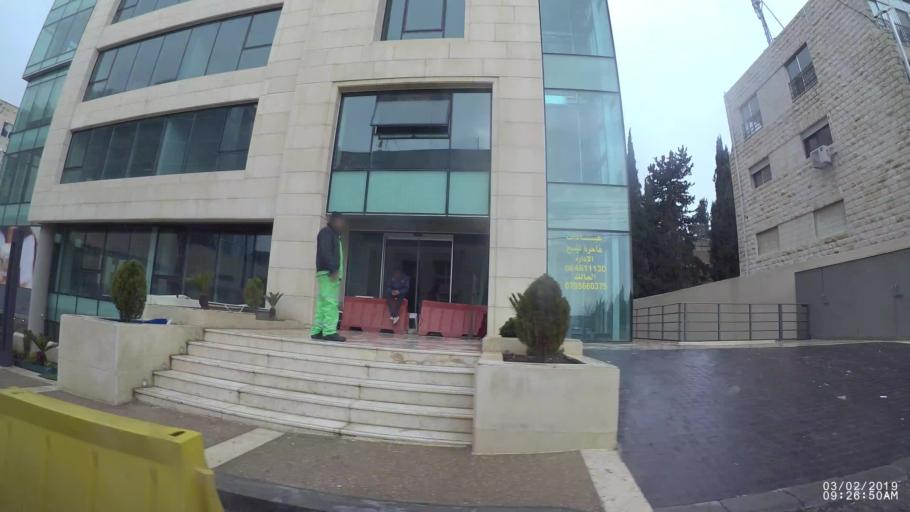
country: JO
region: Amman
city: Amman
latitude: 31.9523
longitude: 35.9054
